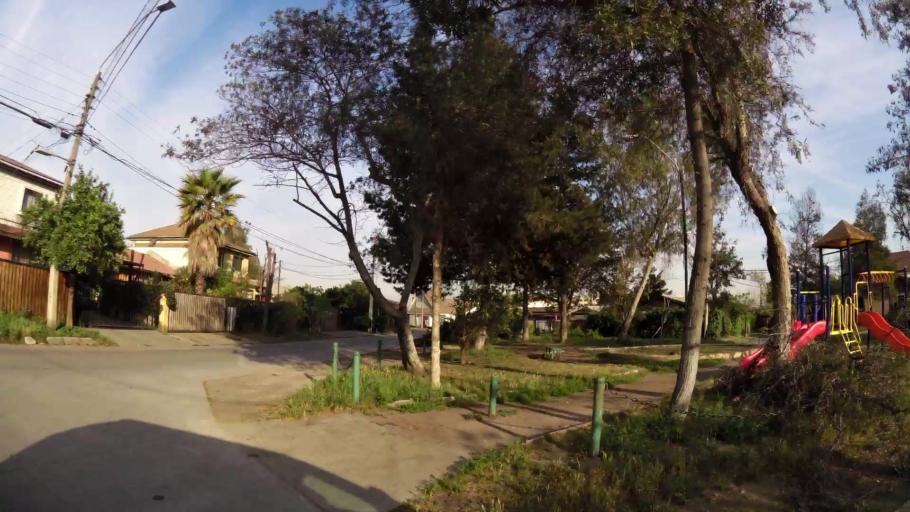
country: CL
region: Santiago Metropolitan
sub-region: Provincia de Santiago
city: La Pintana
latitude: -33.5279
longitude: -70.6749
